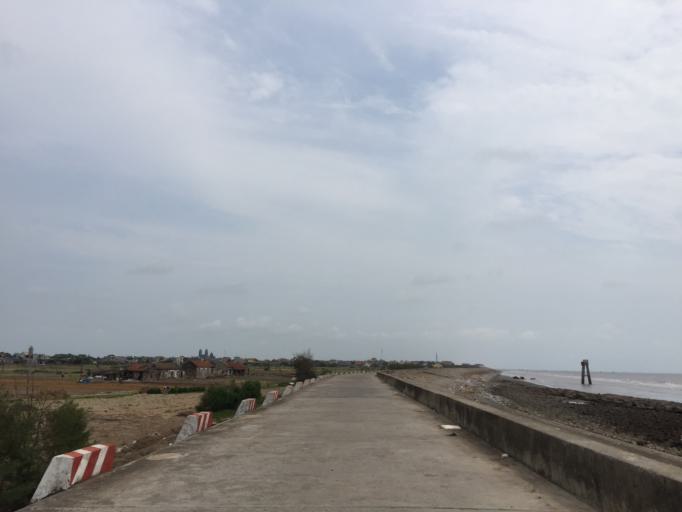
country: VN
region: Ninh Binh
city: Thi Tran Phat Diem
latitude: 20.0124
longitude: 106.2078
